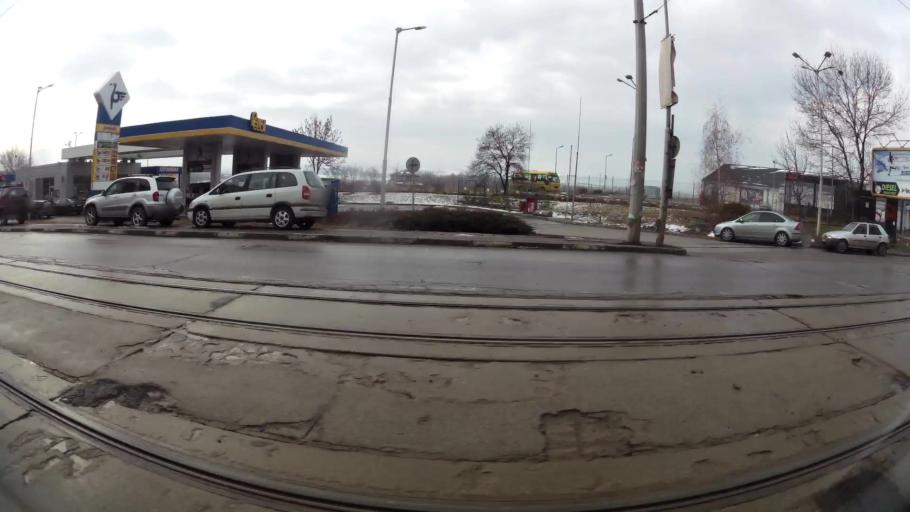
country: BG
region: Sofiya
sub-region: Obshtina Bozhurishte
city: Bozhurishte
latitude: 42.7120
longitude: 23.2408
